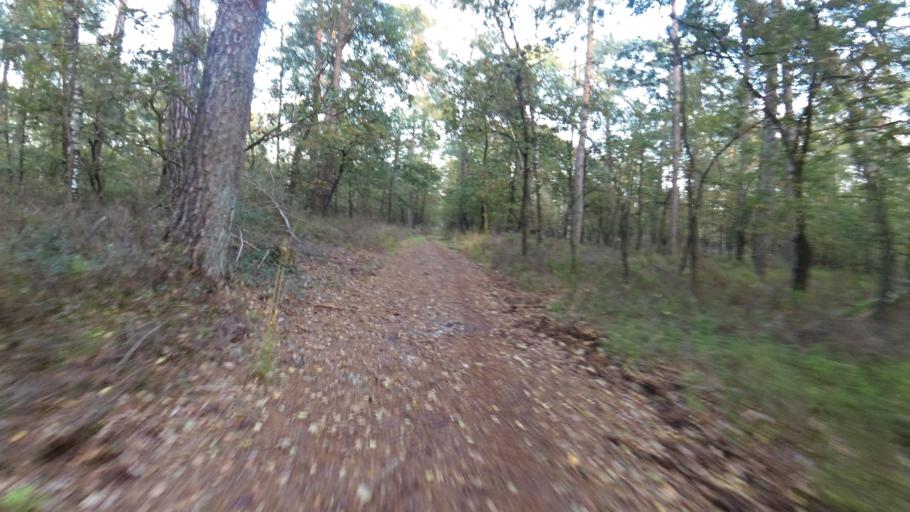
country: NL
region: Gelderland
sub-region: Gemeente Apeldoorn
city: Uddel
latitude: 52.2720
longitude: 5.8047
